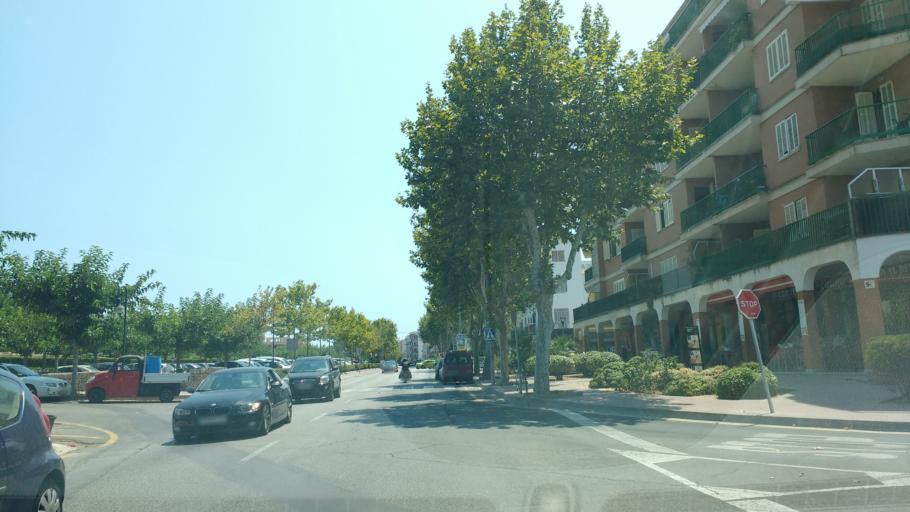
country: ES
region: Balearic Islands
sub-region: Illes Balears
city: Port d'Alcudia
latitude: 39.8444
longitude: 3.1328
